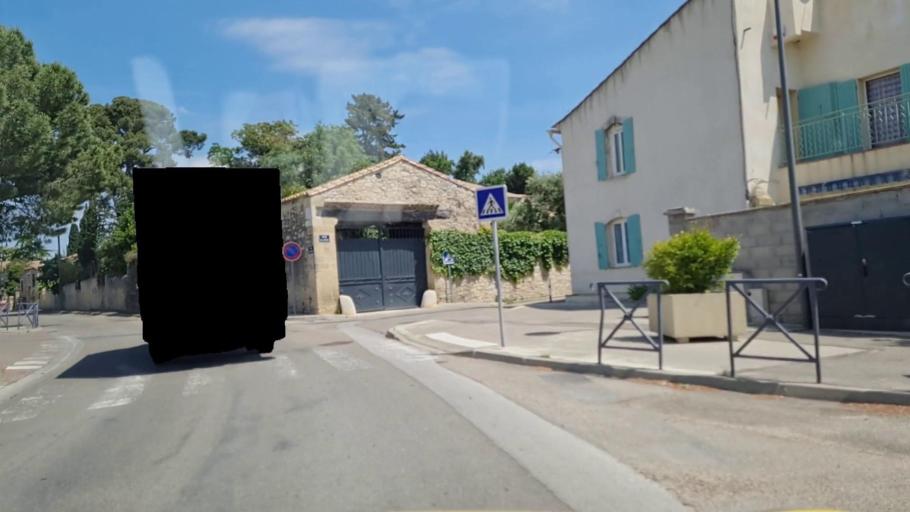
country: FR
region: Languedoc-Roussillon
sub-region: Departement du Gard
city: Saint-Gervasy
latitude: 43.8765
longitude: 4.4674
